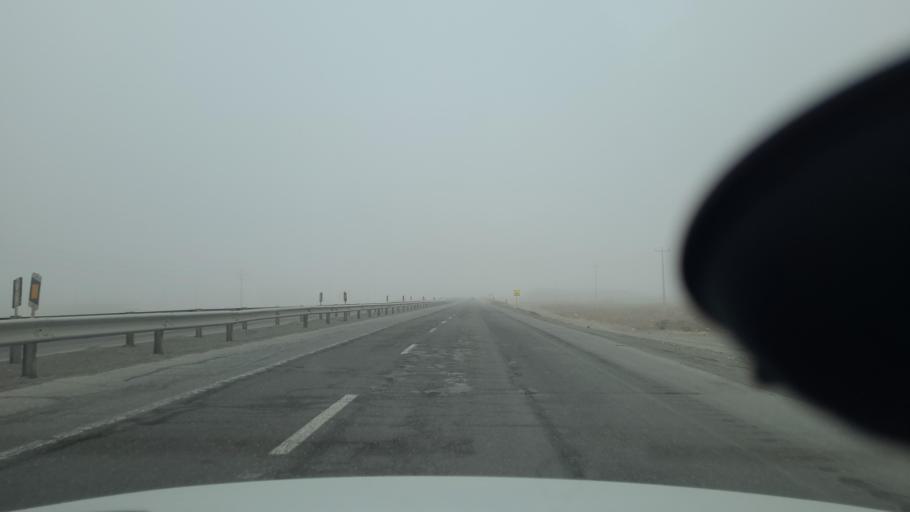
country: IR
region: Razavi Khorasan
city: Fariman
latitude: 35.7640
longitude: 59.7460
